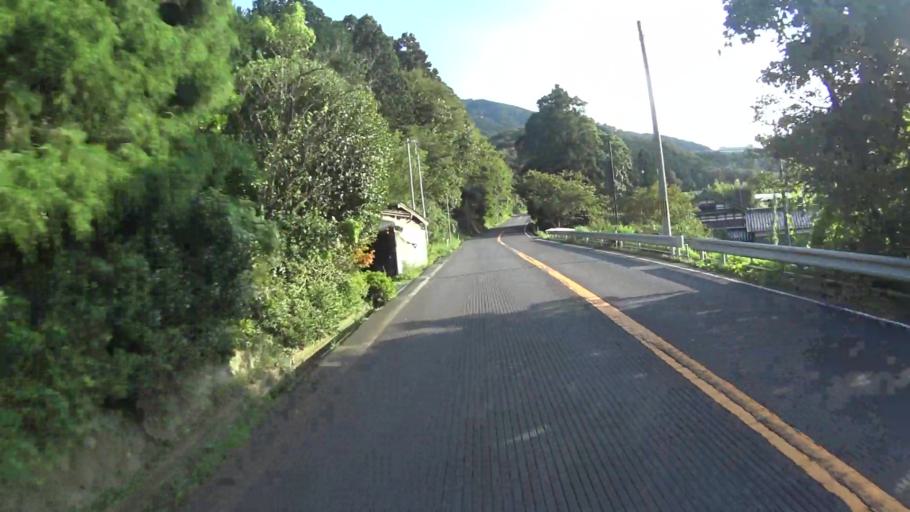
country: JP
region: Kyoto
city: Miyazu
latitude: 35.4630
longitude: 135.0836
